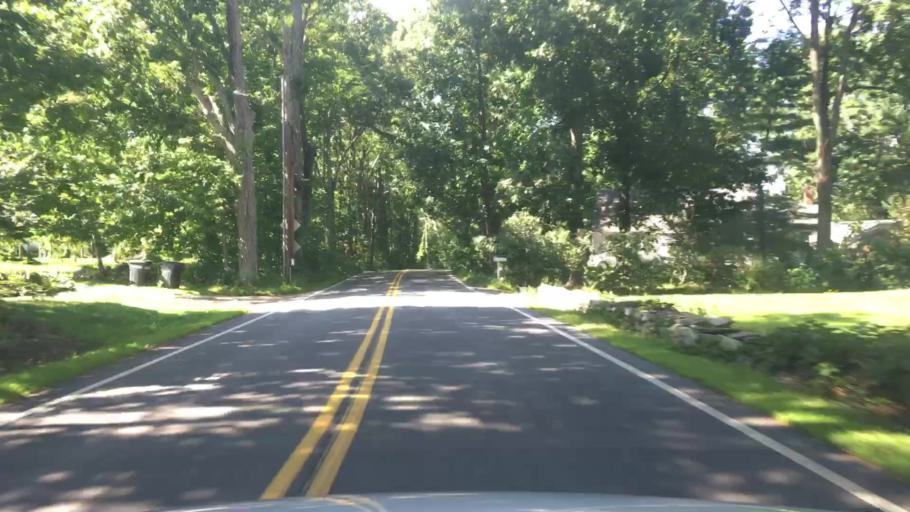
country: US
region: New Hampshire
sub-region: Strafford County
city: Dover
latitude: 43.1795
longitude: -70.8379
